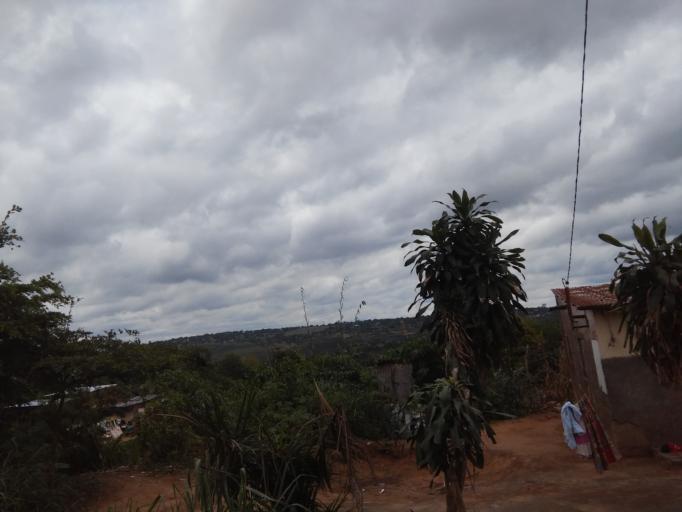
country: CD
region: Kinshasa
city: Masina
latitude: -4.4232
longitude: 15.3324
